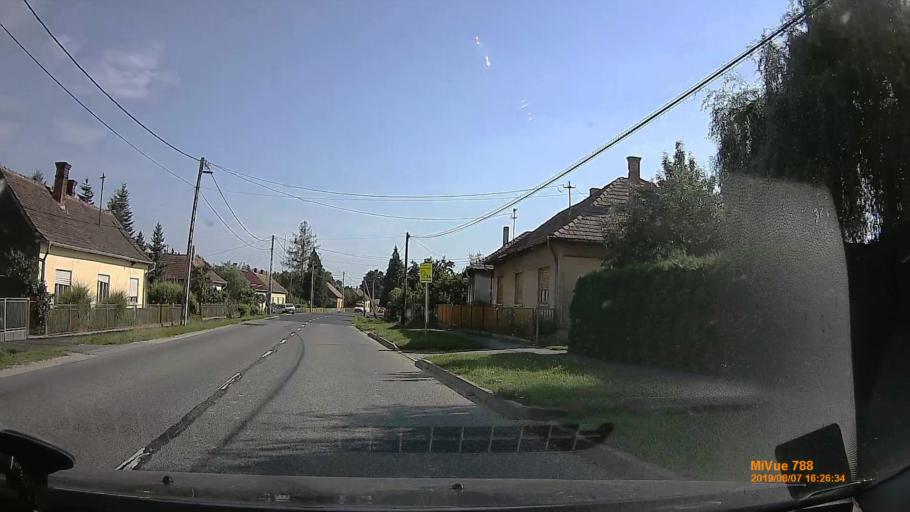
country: HU
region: Zala
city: Lenti
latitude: 46.7089
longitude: 16.5520
